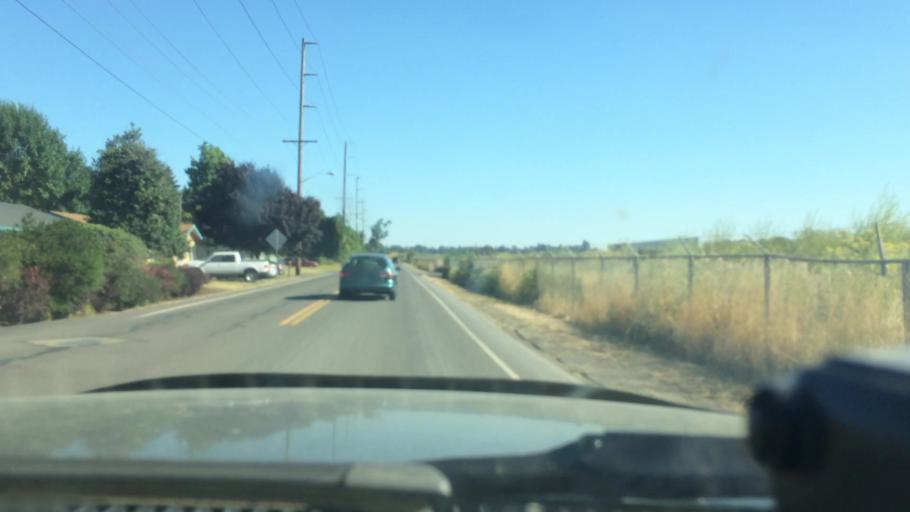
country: US
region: Oregon
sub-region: Lane County
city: Eugene
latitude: 44.0985
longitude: -123.1142
